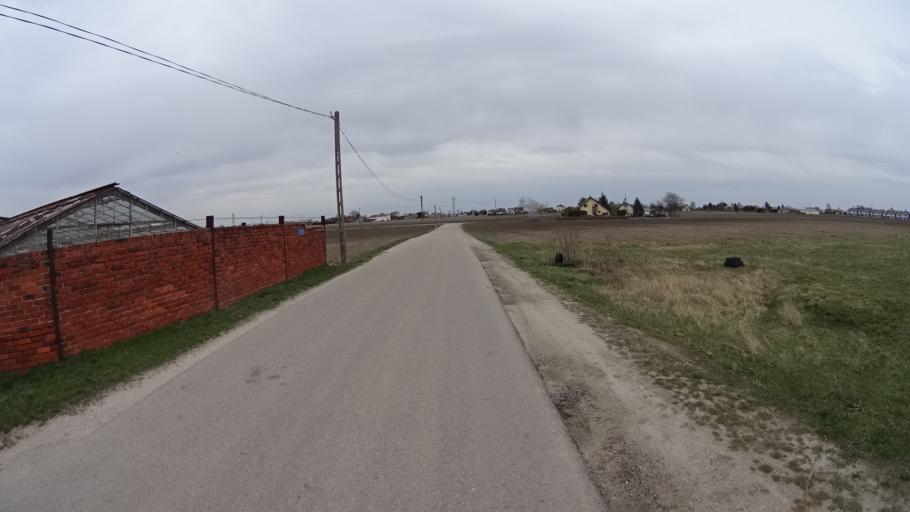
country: PL
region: Masovian Voivodeship
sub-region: Powiat warszawski zachodni
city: Stare Babice
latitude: 52.2425
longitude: 20.8225
